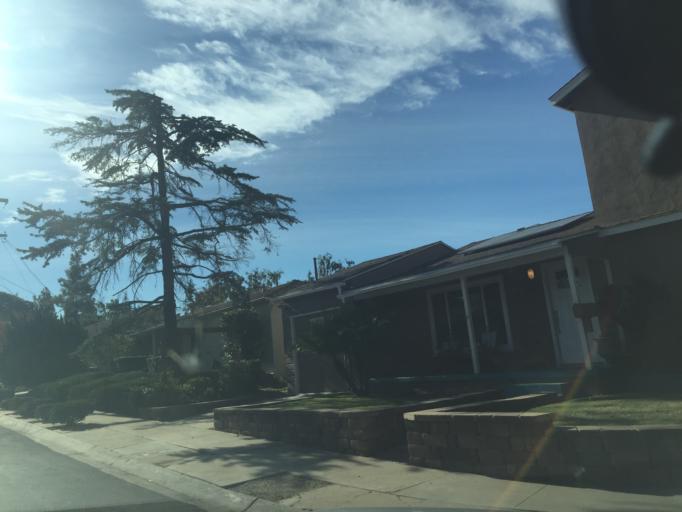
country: US
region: California
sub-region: San Diego County
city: Lemon Grove
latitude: 32.7636
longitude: -117.0828
